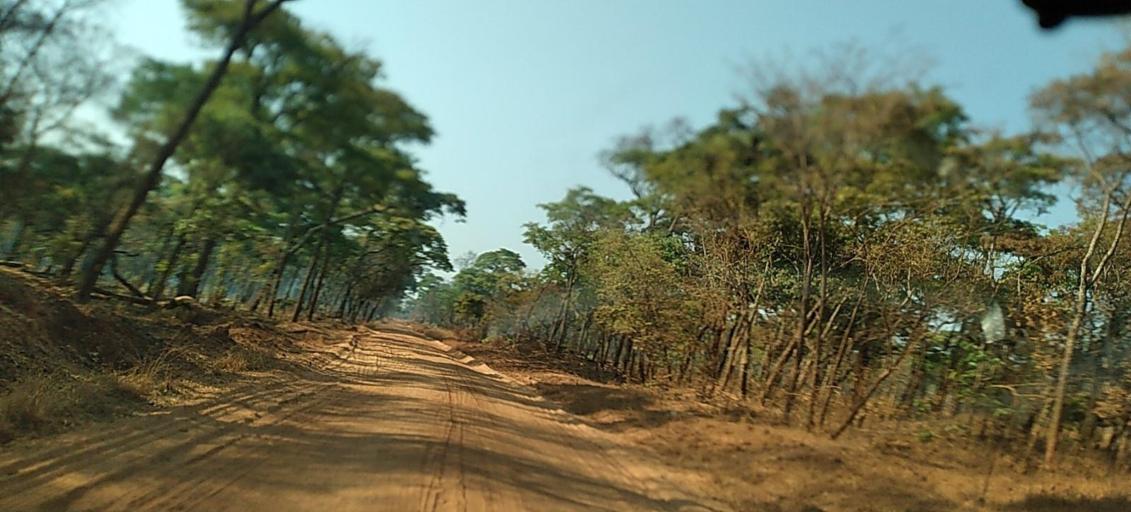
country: ZM
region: North-Western
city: Kasempa
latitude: -13.6166
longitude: 25.9795
